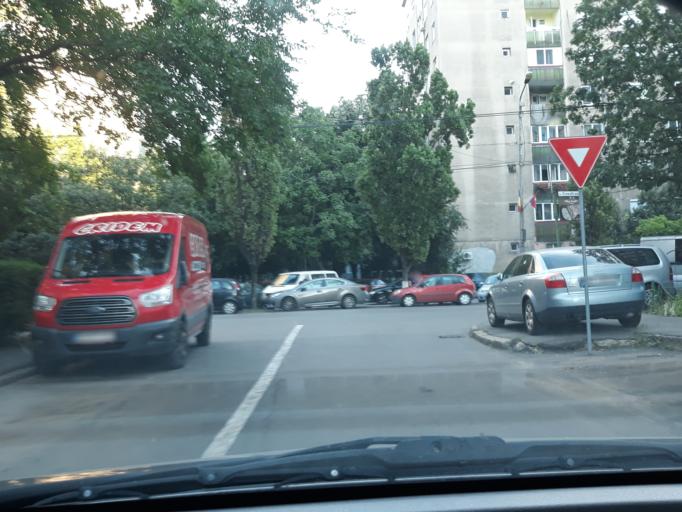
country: RO
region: Bihor
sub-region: Comuna Biharea
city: Oradea
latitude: 47.0797
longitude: 21.9192
